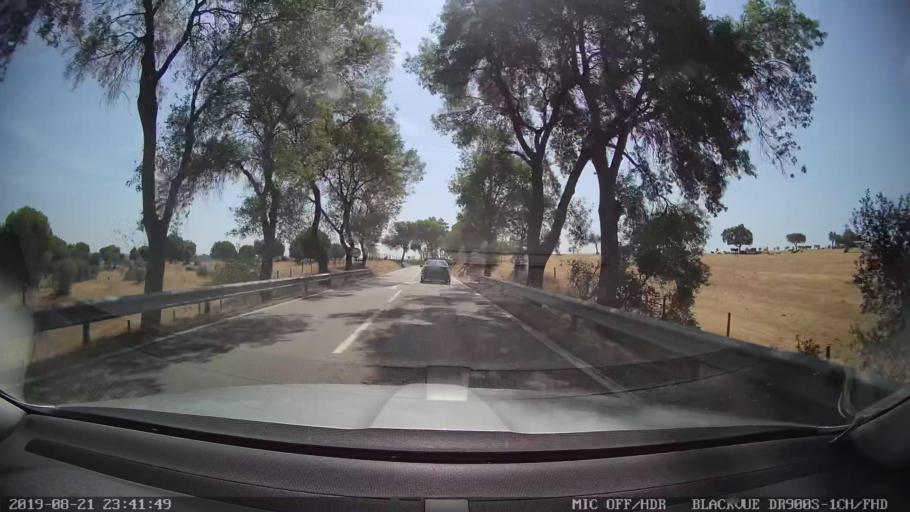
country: PT
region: Castelo Branco
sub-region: Idanha-A-Nova
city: Idanha-a-Nova
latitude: 39.8620
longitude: -7.3179
